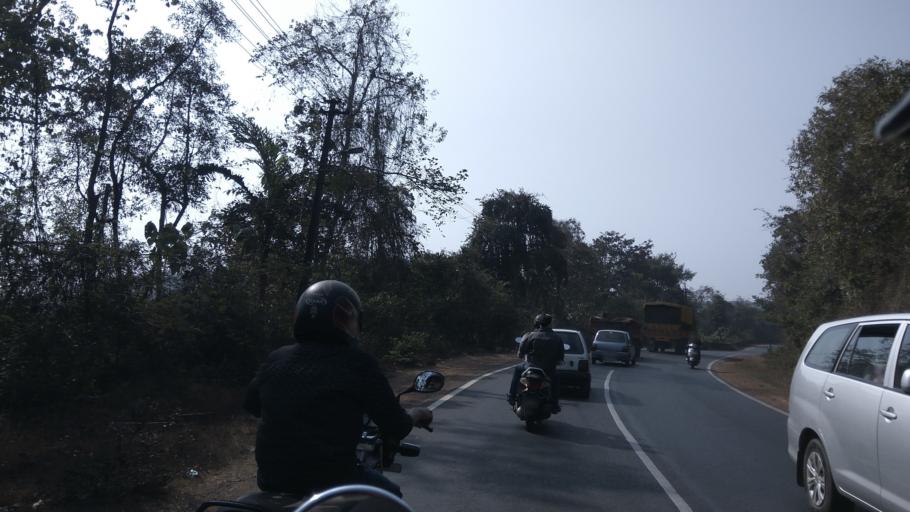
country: IN
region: Goa
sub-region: North Goa
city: Bandora
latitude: 15.4257
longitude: 73.9872
